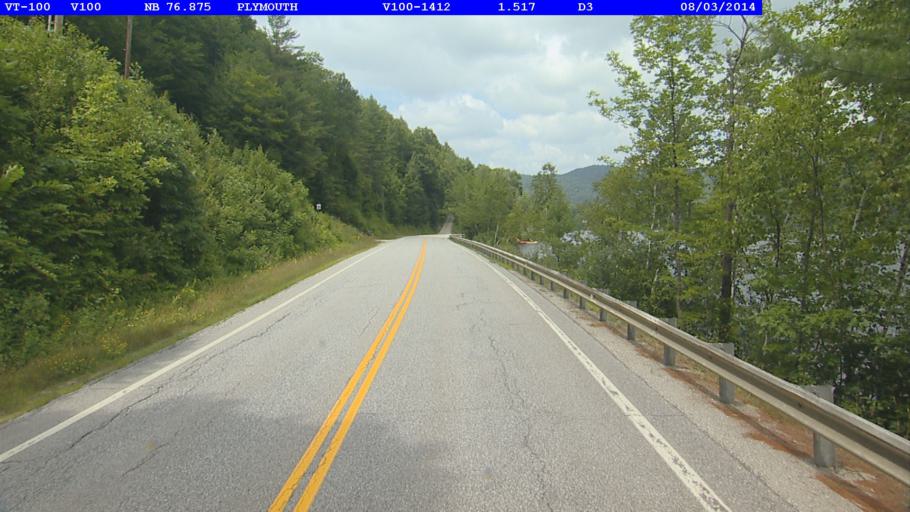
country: US
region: Vermont
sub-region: Windsor County
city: Woodstock
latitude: 43.4843
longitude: -72.7054
